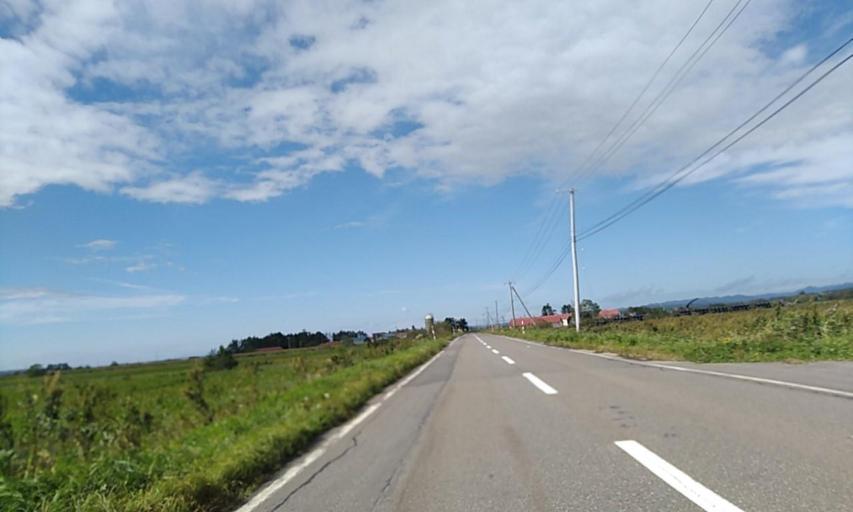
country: JP
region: Hokkaido
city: Obihiro
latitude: 42.7187
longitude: 143.6347
